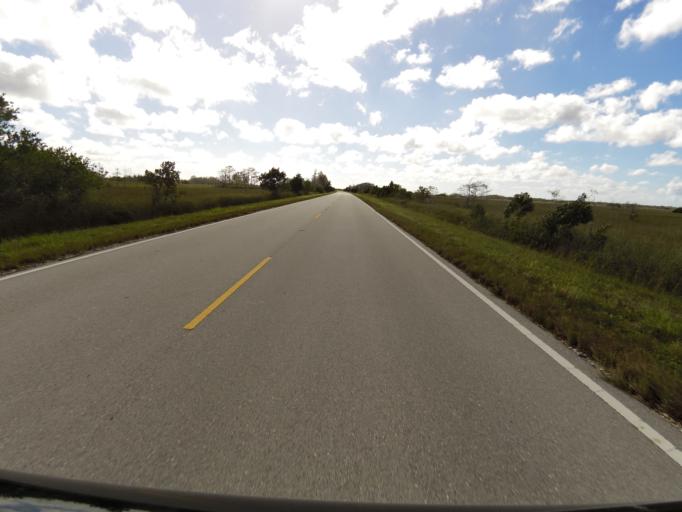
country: US
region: Florida
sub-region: Miami-Dade County
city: Florida City
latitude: 25.3794
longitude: -80.8119
